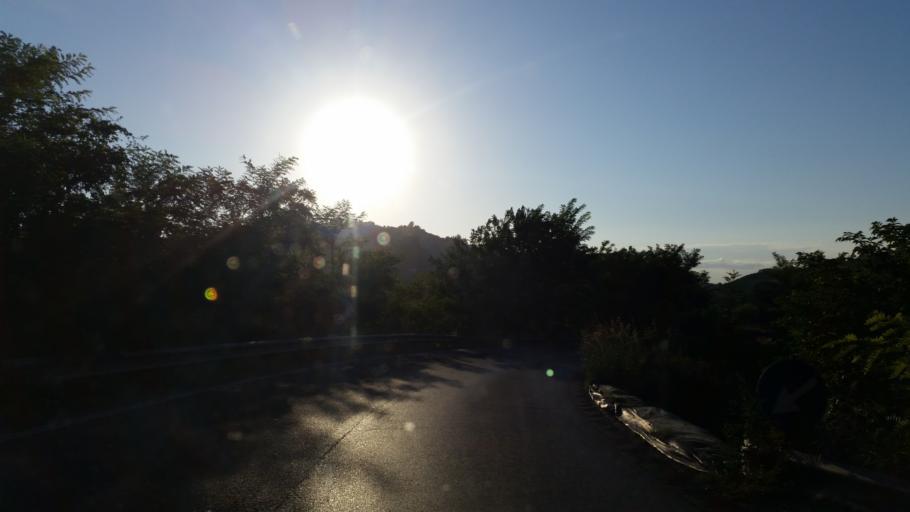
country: IT
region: Piedmont
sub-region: Provincia di Cuneo
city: Santo Stefano Belbo
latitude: 44.7118
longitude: 8.2483
